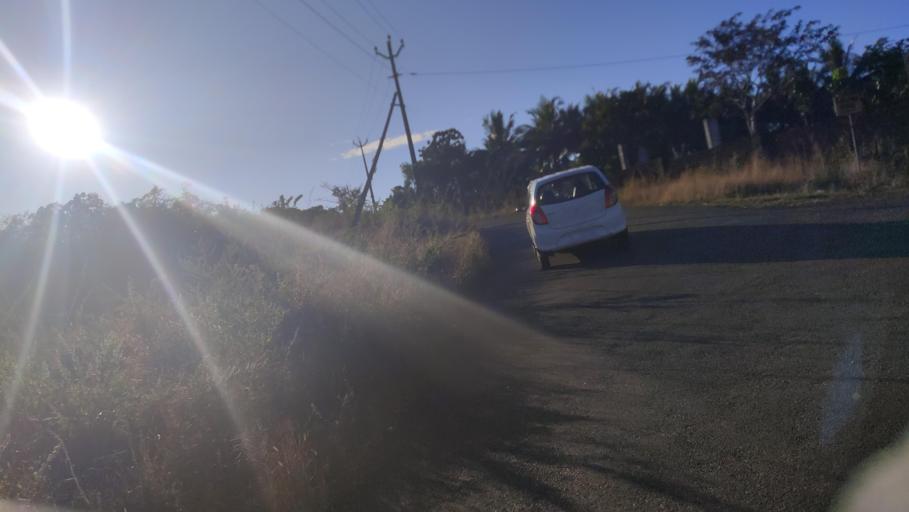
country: IN
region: Kerala
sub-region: Kasaragod District
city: Kasaragod
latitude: 12.4973
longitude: 75.0805
